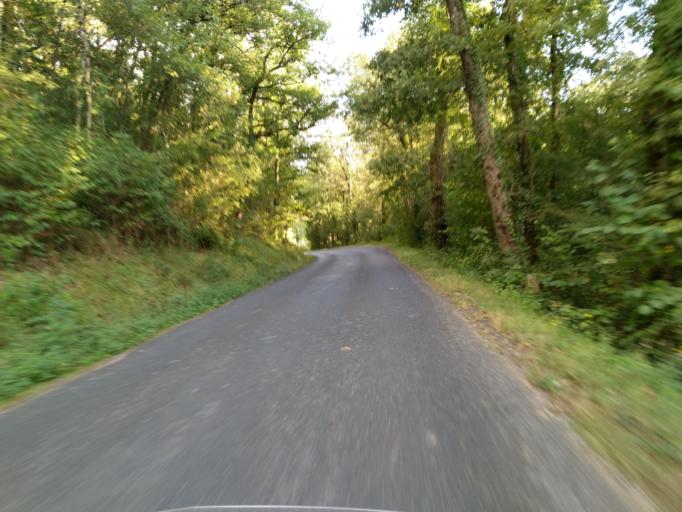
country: FR
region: Midi-Pyrenees
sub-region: Departement du Tarn
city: Frejairolles
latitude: 43.8570
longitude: 2.2349
